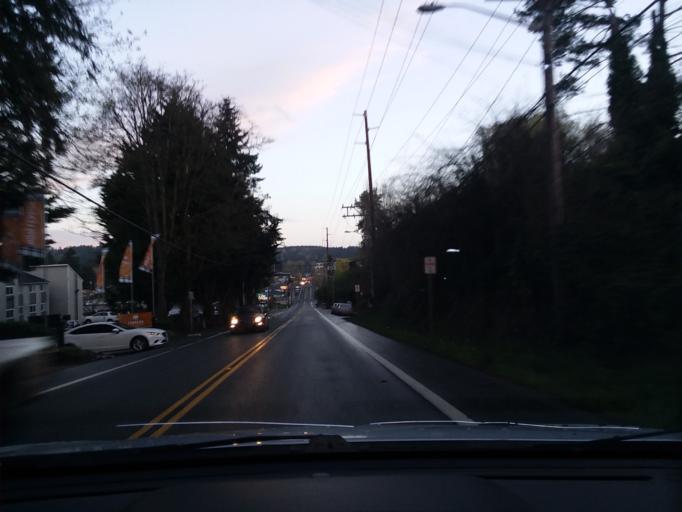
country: US
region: Washington
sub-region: King County
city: Kenmore
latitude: 47.7653
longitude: -122.2496
